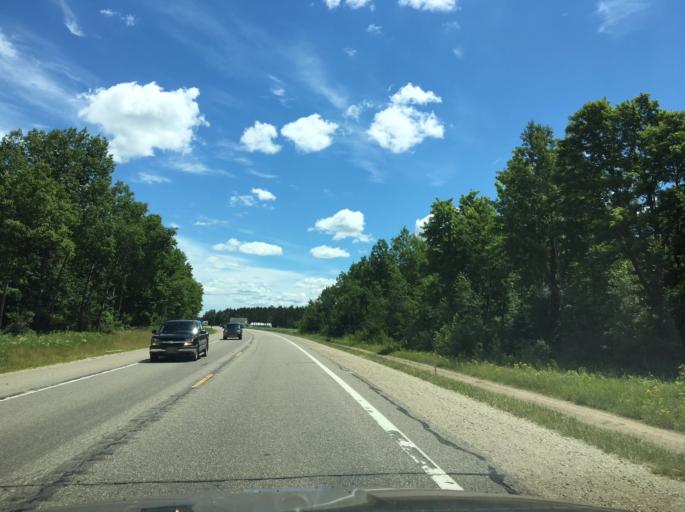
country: US
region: Michigan
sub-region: Osceola County
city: Reed City
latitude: 43.8727
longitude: -85.3936
